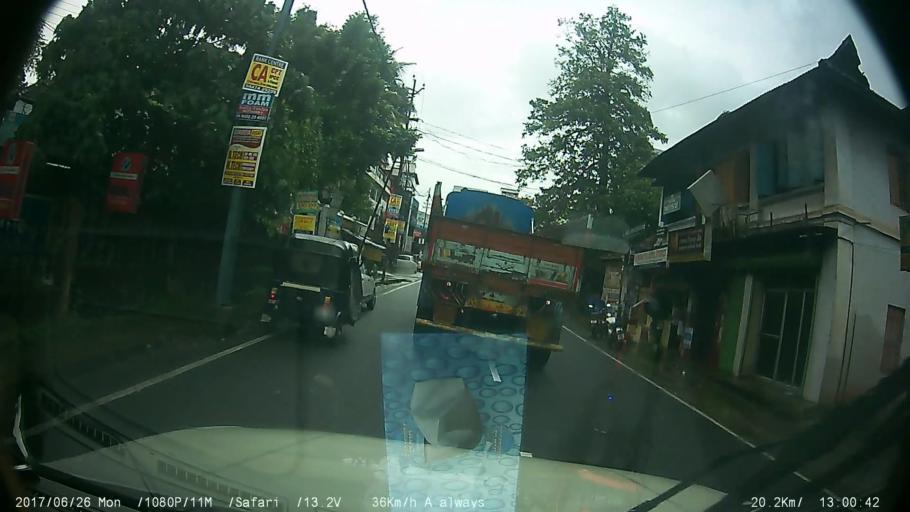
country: IN
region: Kerala
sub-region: Kottayam
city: Kottayam
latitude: 9.5873
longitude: 76.5215
